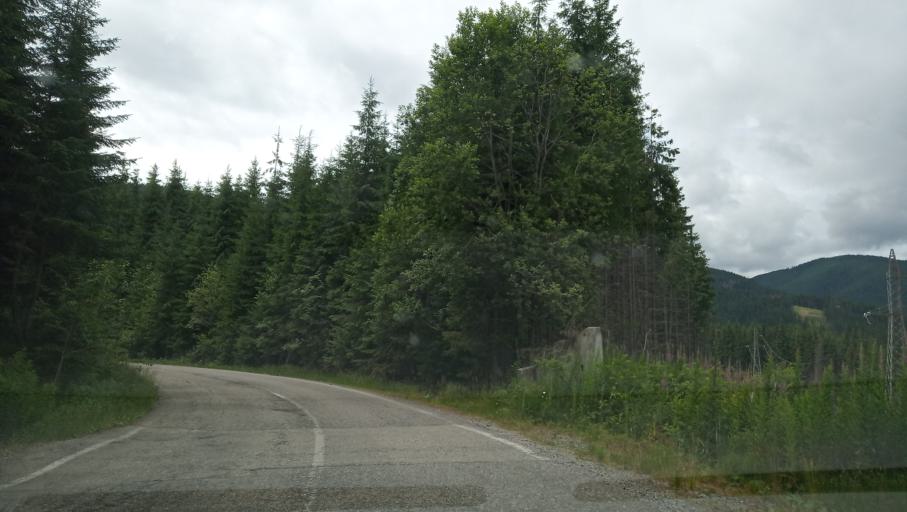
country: RO
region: Valcea
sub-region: Comuna Voineasa
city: Voineasa
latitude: 45.4178
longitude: 23.7197
